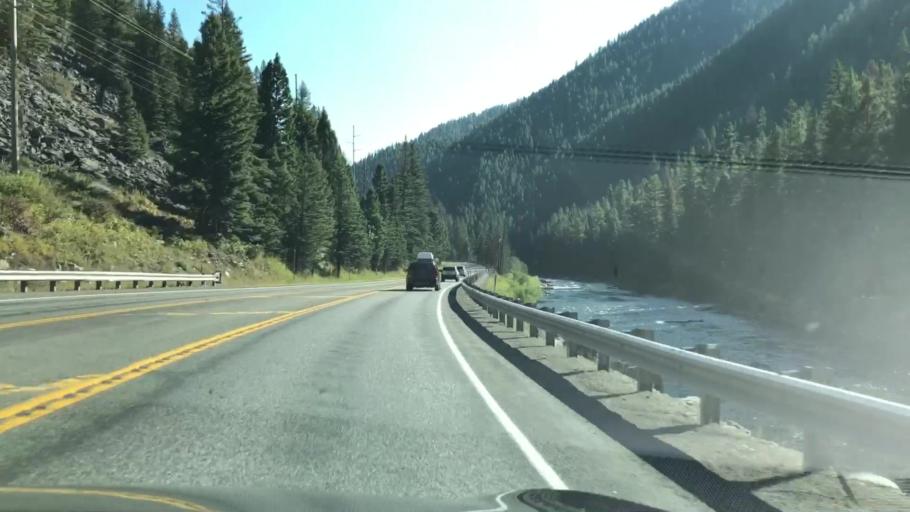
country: US
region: Montana
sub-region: Gallatin County
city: Big Sky
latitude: 45.3710
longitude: -111.1747
